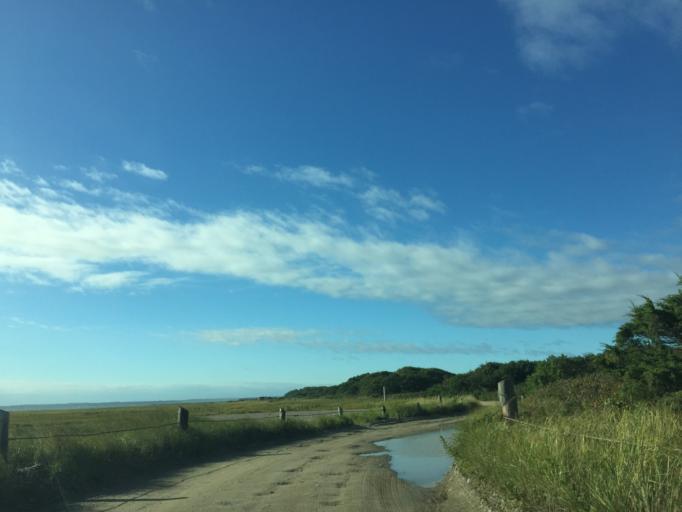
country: US
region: Massachusetts
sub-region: Plymouth County
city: Duxbury
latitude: 42.0105
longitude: -70.6083
